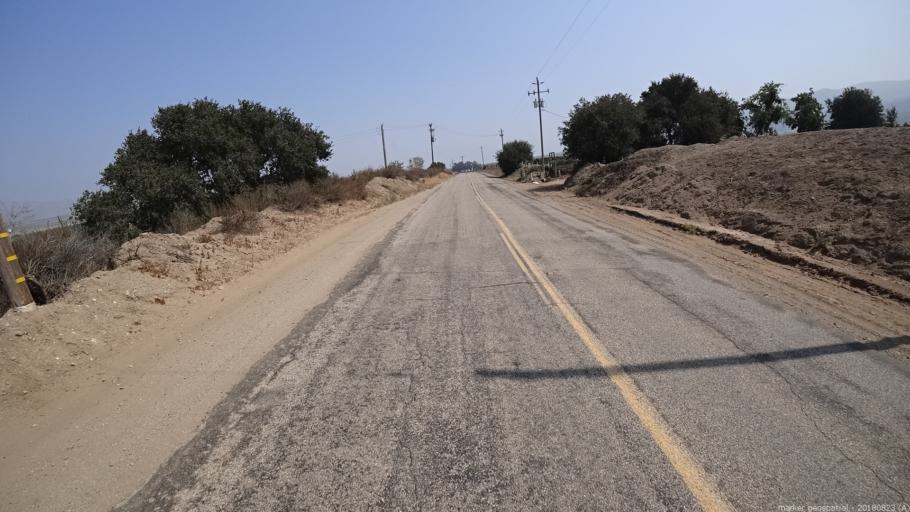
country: US
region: California
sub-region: Monterey County
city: Gonzales
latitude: 36.4529
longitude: -121.4410
